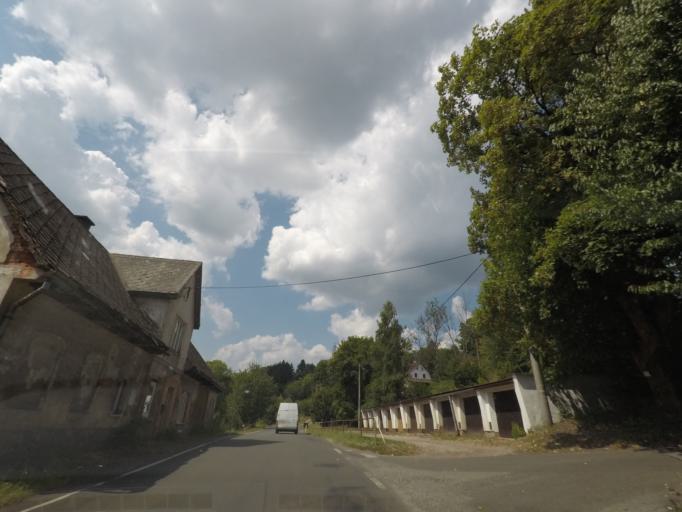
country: CZ
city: Radvanice
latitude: 50.5989
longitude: 16.0338
